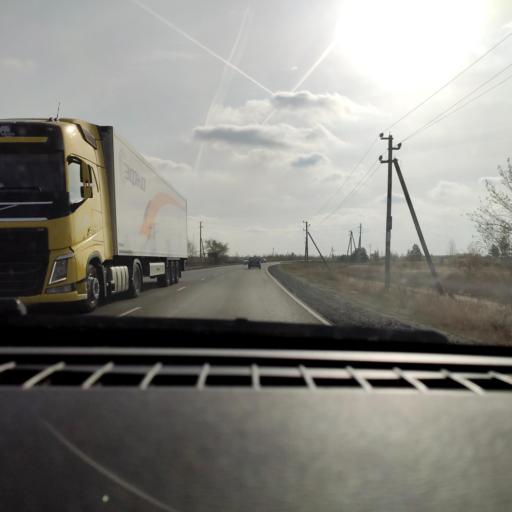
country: RU
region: Voronezj
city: Maslovka
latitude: 51.5788
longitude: 39.2647
